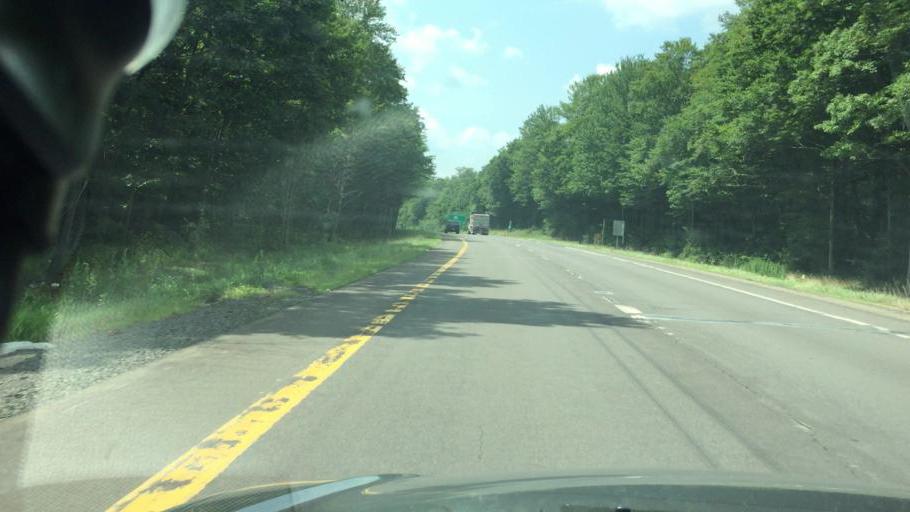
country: US
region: Pennsylvania
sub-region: Luzerne County
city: White Haven
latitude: 41.0602
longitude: -75.7399
